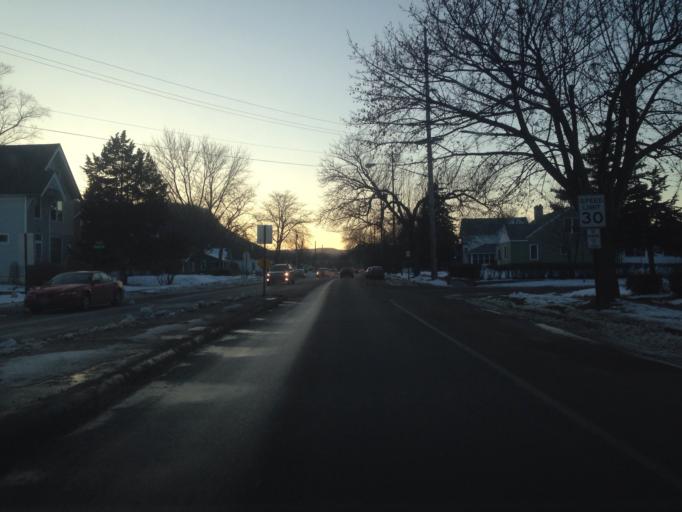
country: US
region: Minnesota
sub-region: Winona County
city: Winona
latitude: 44.0486
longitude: -91.6621
